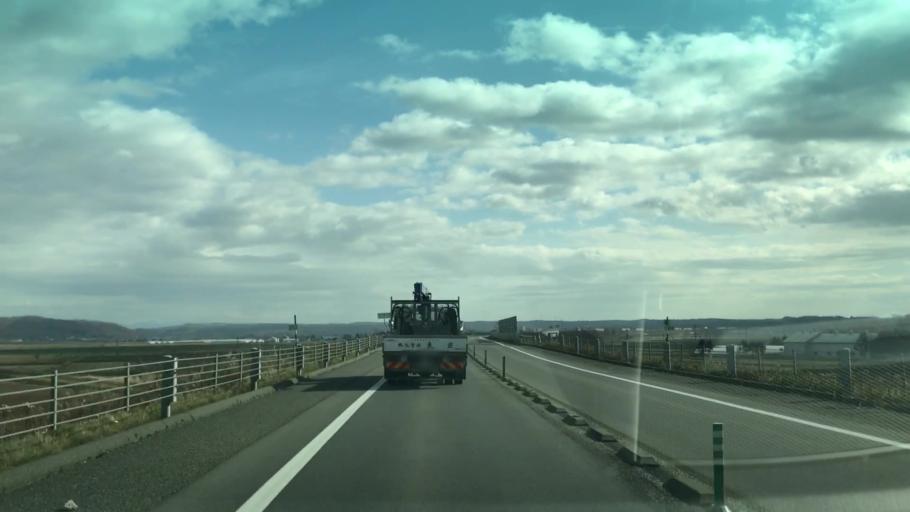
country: JP
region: Hokkaido
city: Tomakomai
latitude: 42.5775
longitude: 141.9619
